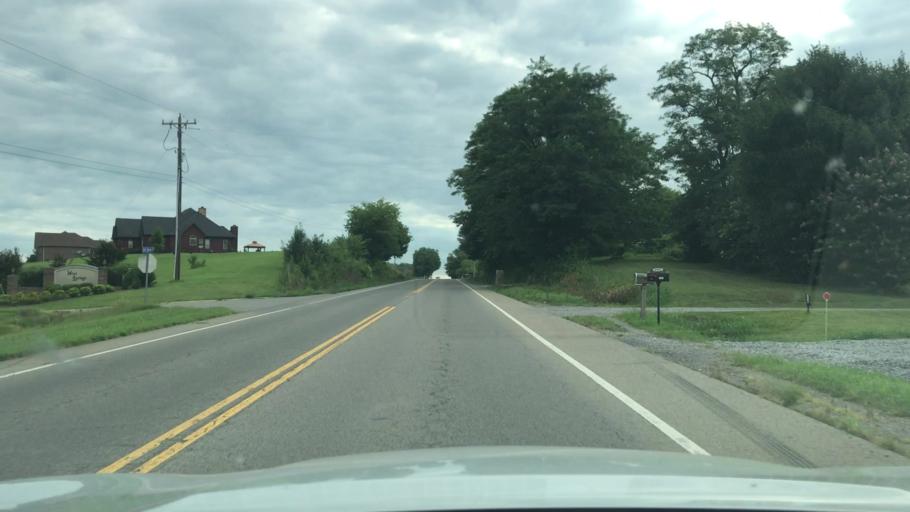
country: US
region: Kentucky
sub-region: Todd County
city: Guthrie
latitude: 36.6285
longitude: -87.2187
